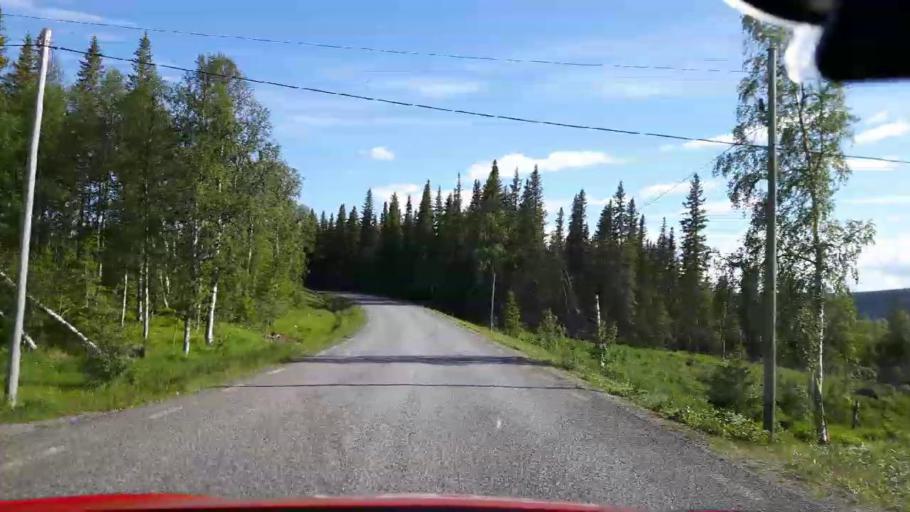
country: SE
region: Jaemtland
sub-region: Krokoms Kommun
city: Valla
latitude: 63.7238
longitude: 14.1227
